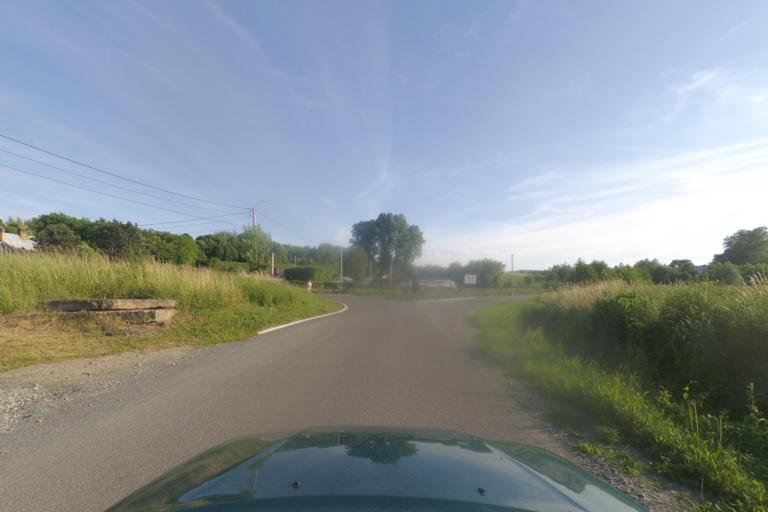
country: PL
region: Lower Silesian Voivodeship
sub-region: Powiat dzierzoniowski
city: Niemcza
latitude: 50.7156
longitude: 16.8308
